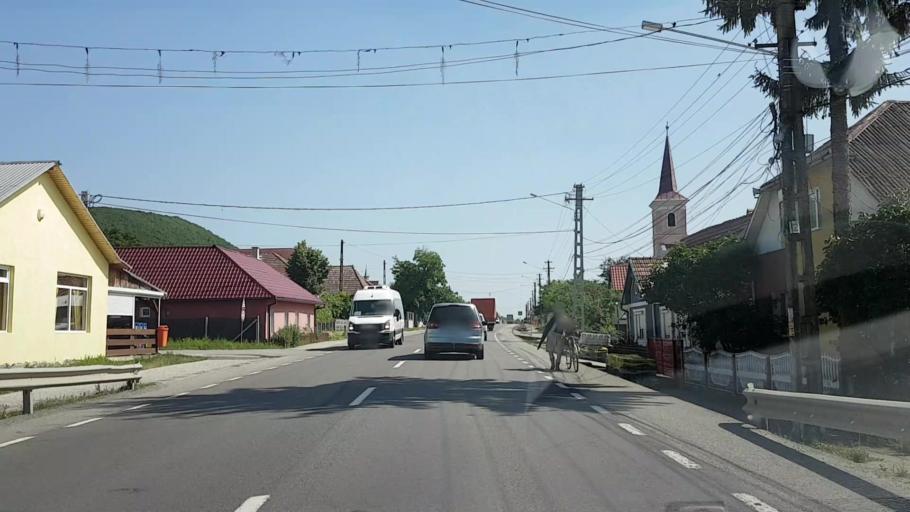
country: RO
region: Bistrita-Nasaud
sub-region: Comuna Sieu-Odorhei
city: Sieu-Odorhei
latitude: 47.1473
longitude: 24.3061
